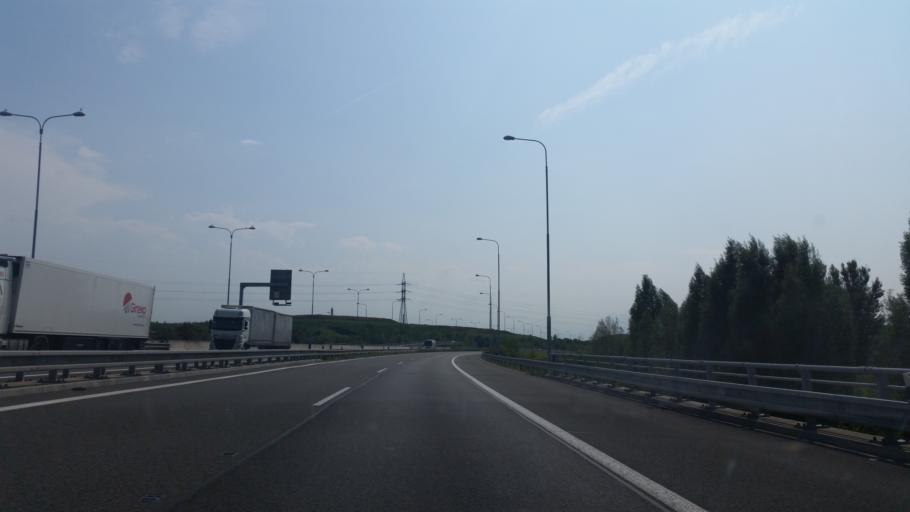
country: PL
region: Silesian Voivodeship
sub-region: Powiat raciborski
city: Chalupki
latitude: 49.8807
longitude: 18.3053
